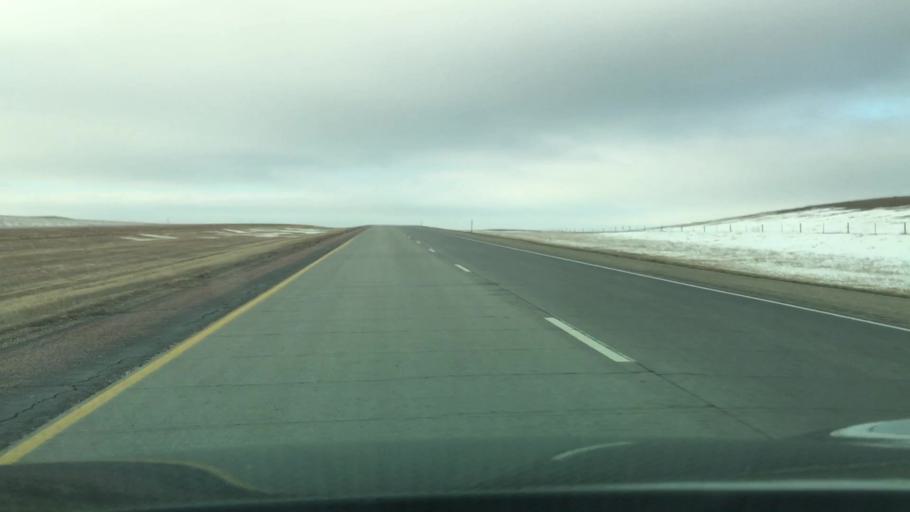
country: US
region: South Dakota
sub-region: Brule County
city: Chamberlain
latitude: 43.8327
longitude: -99.4662
